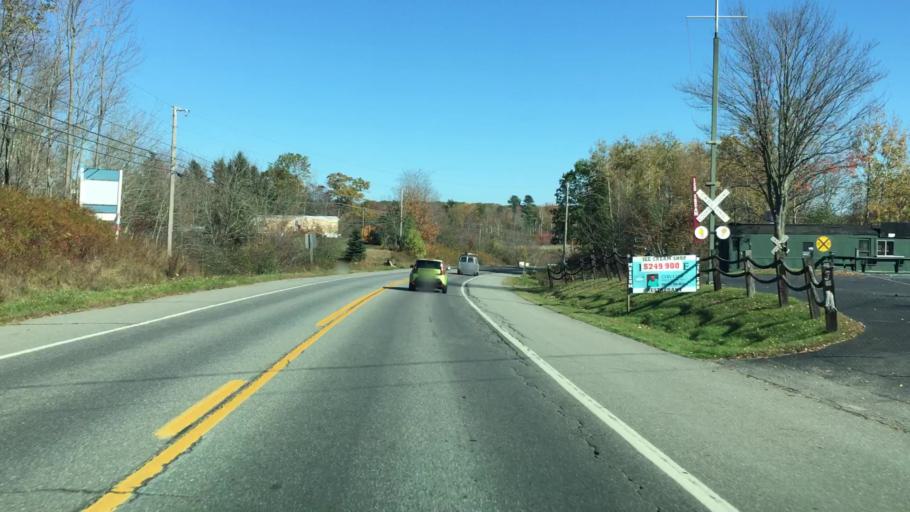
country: US
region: Maine
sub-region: Waldo County
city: Stockton Springs
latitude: 44.4676
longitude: -68.9003
